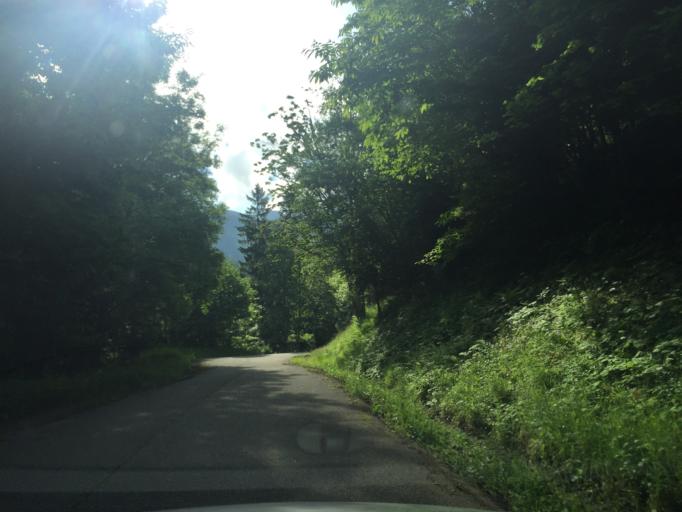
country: FR
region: Rhone-Alpes
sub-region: Departement de la Savoie
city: La Rochette
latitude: 45.4375
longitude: 6.1532
